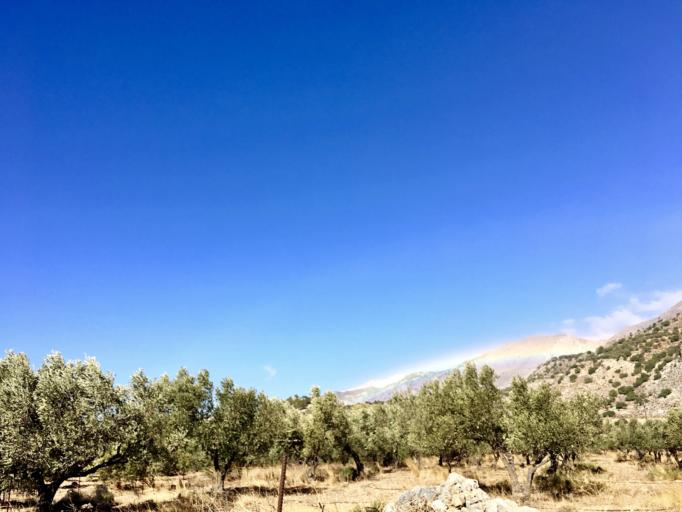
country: GR
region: Crete
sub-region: Nomos Chanias
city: Chora Sfakion
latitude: 35.1983
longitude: 24.2251
